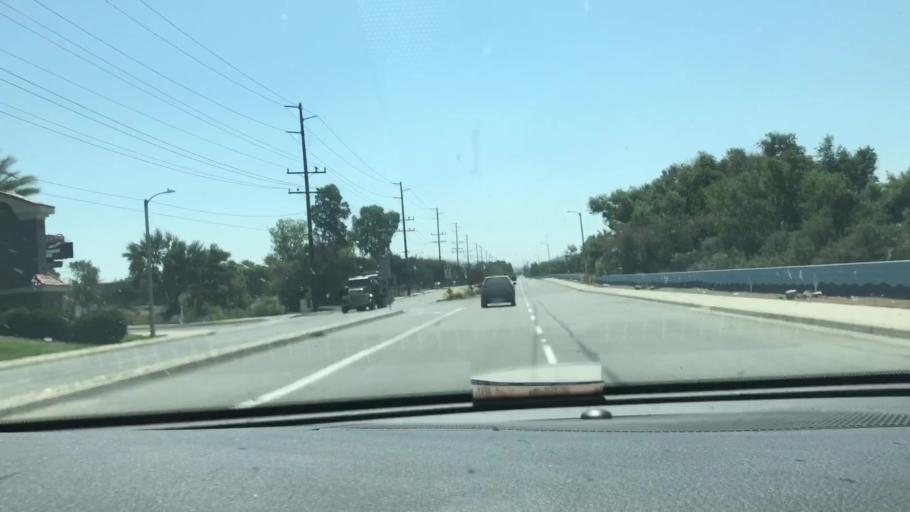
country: US
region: California
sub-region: Riverside County
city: Lake Elsinore
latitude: 33.7039
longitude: -117.3575
